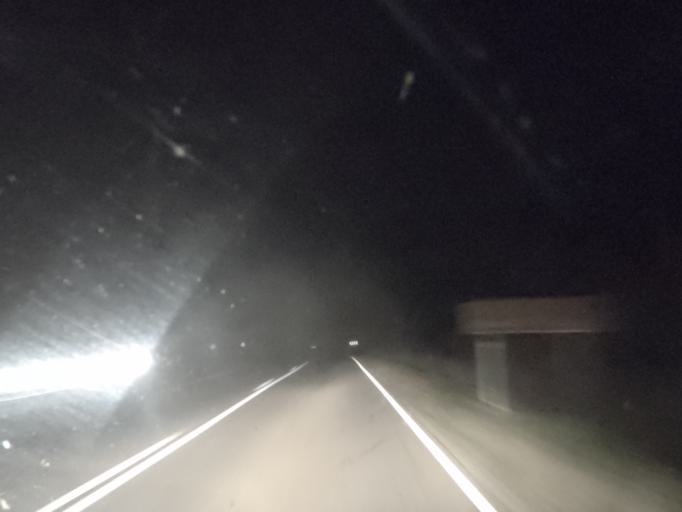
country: ES
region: Castille and Leon
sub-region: Provincia de Zamora
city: Santa Cristina de la Polvorosa
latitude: 42.0254
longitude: -5.7020
